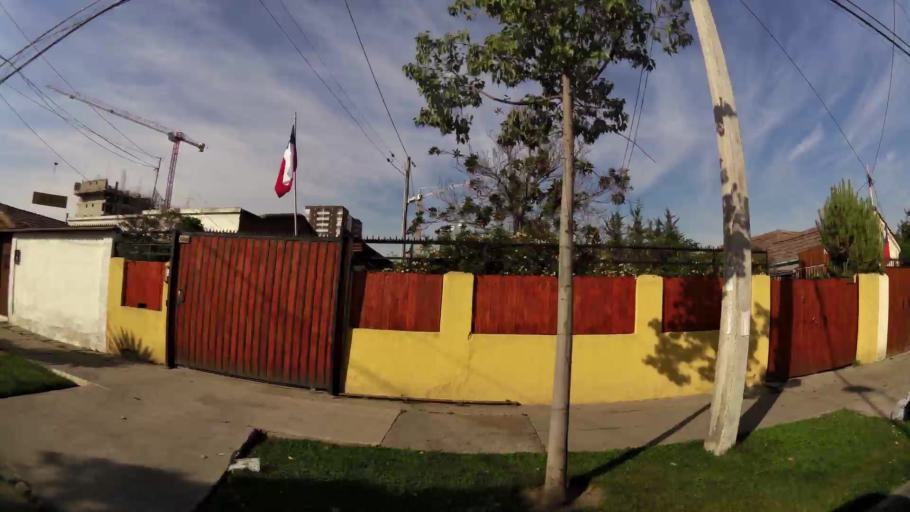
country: CL
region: Santiago Metropolitan
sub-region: Provincia de Santiago
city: Santiago
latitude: -33.5043
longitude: -70.6633
